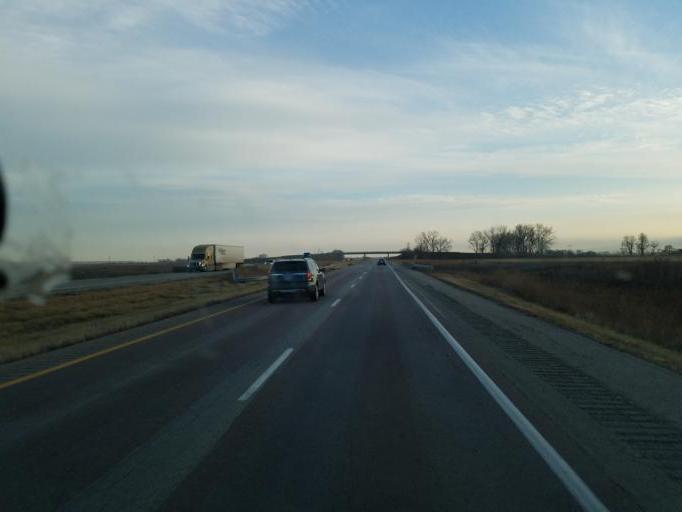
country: US
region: Nebraska
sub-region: Washington County
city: Blair
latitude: 41.6724
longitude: -96.0368
